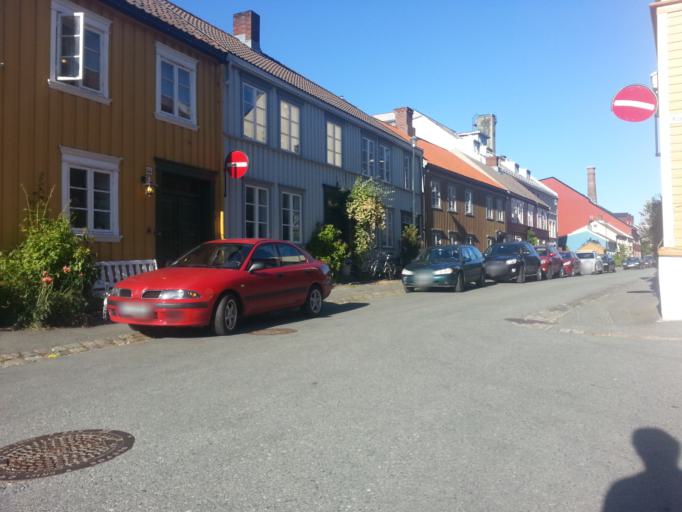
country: NO
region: Sor-Trondelag
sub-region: Trondheim
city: Trondheim
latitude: 63.4312
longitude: 10.3667
